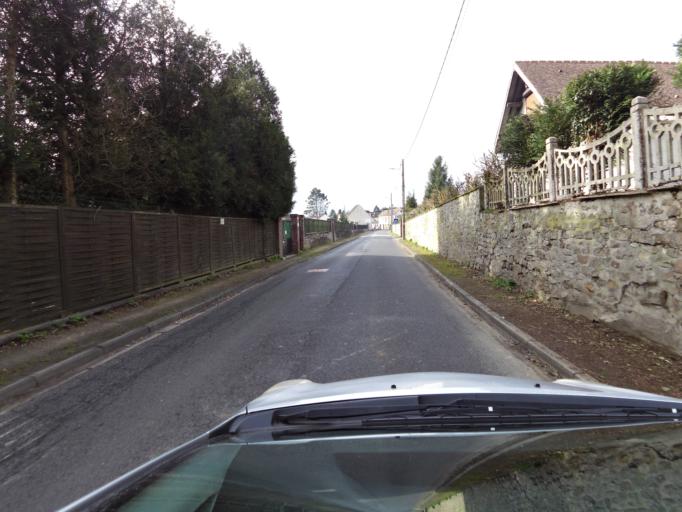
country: FR
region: Picardie
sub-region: Departement de l'Oise
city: Ver-sur-Launette
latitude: 49.1089
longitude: 2.6854
